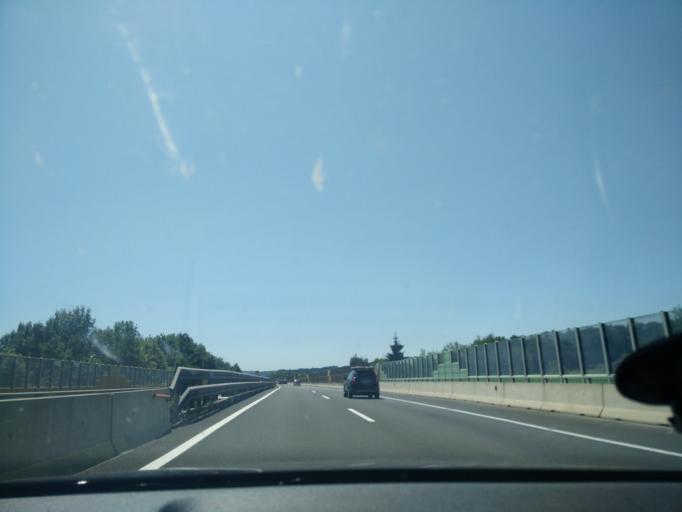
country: AT
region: Styria
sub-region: Politischer Bezirk Hartberg-Fuerstenfeld
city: Sankt Johann in der Haide
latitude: 47.2424
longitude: 15.9964
